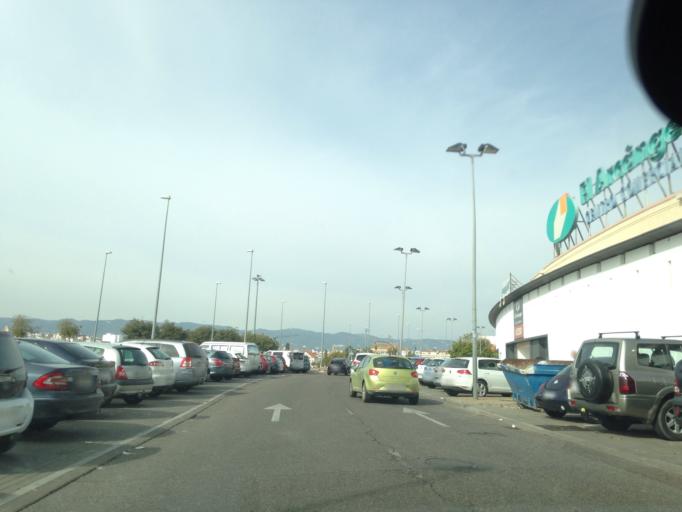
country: ES
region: Andalusia
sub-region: Province of Cordoba
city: Cordoba
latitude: 37.8774
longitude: -4.7670
